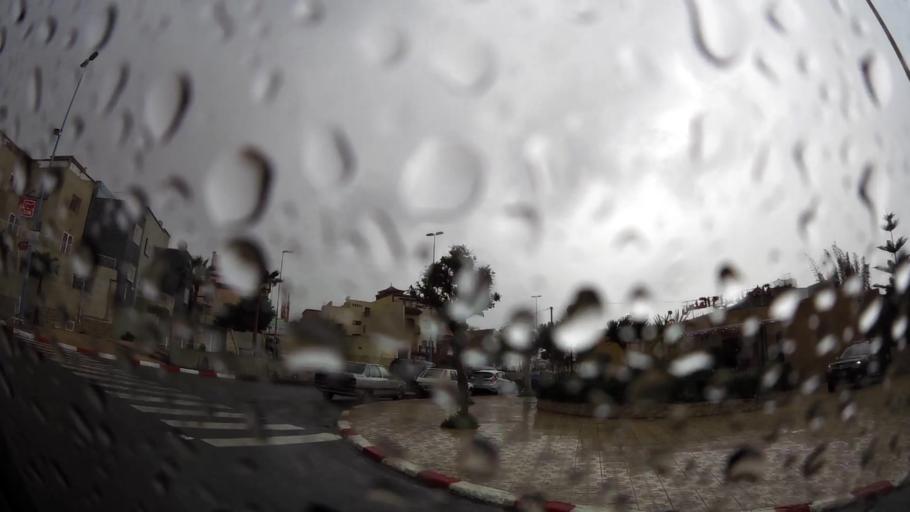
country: MA
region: Grand Casablanca
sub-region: Mediouna
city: Tit Mellil
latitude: 33.6213
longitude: -7.4797
